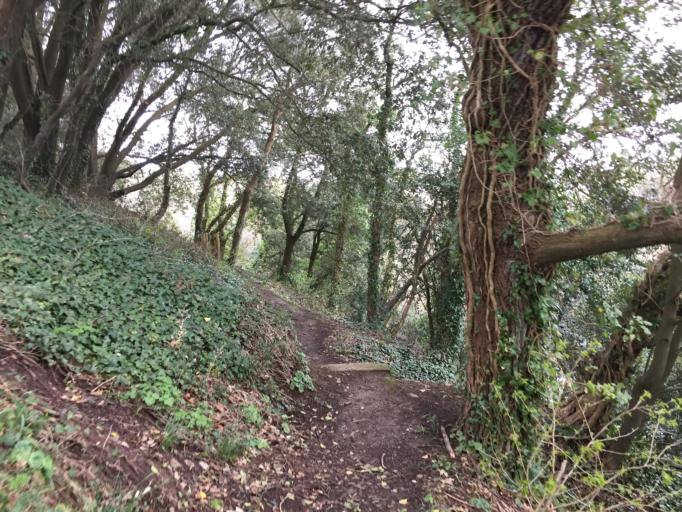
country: JE
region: St Helier
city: Saint Helier
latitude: 49.2165
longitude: -2.1342
